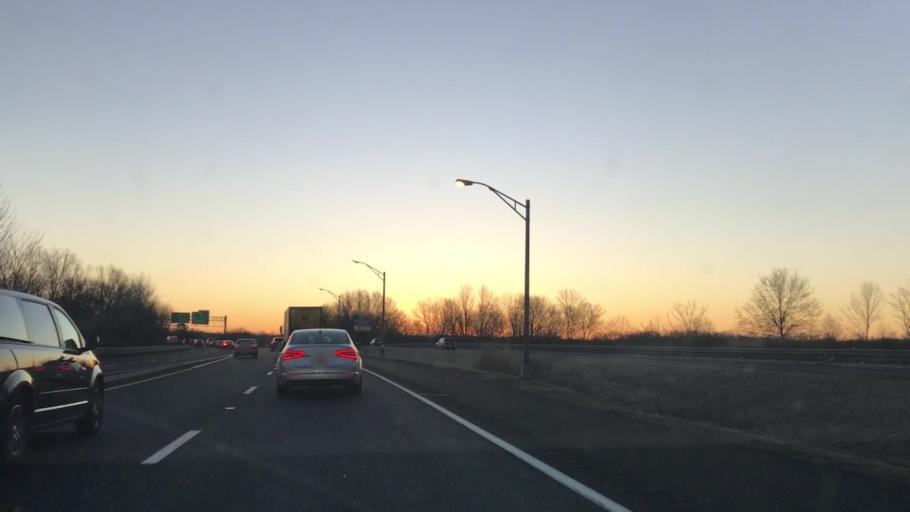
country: US
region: New Jersey
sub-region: Morris County
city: East Hanover
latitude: 40.8584
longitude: -74.3719
